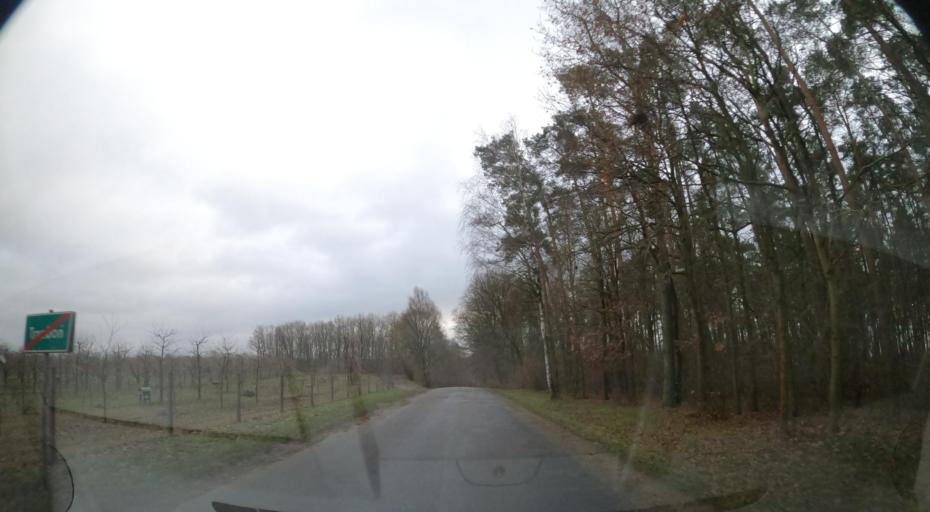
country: PL
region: Greater Poland Voivodeship
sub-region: Powiat pilski
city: Lobzenica
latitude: 53.2369
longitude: 17.3064
